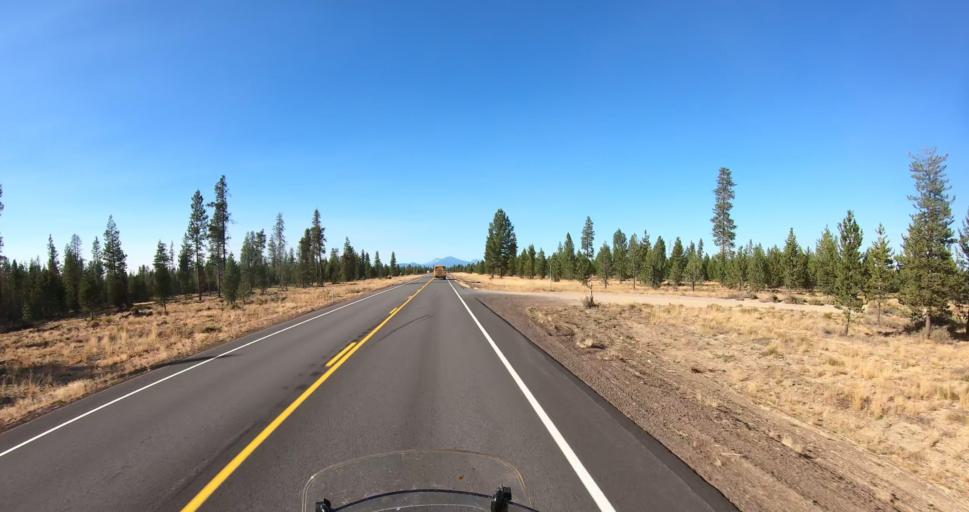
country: US
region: Oregon
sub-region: Deschutes County
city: La Pine
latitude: 43.6019
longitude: -121.4985
